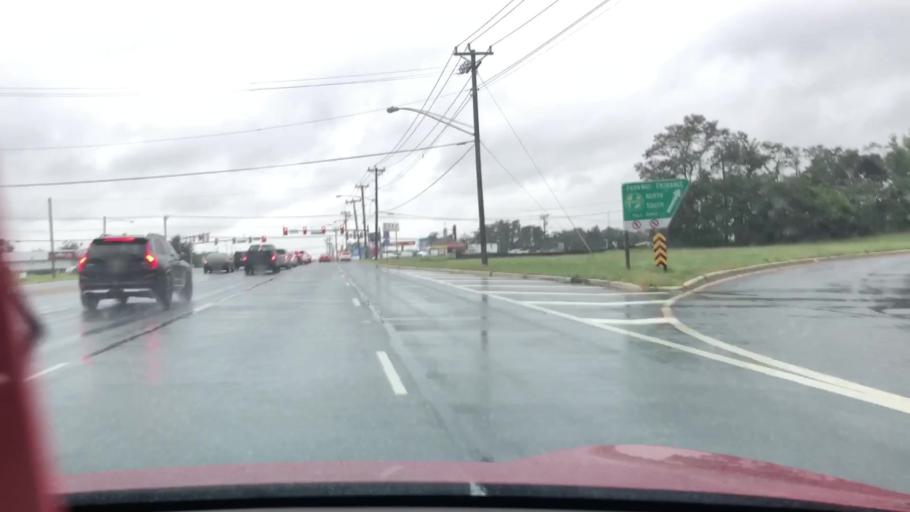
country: US
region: New Jersey
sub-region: Atlantic County
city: Northfield
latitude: 39.3957
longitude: -74.5601
